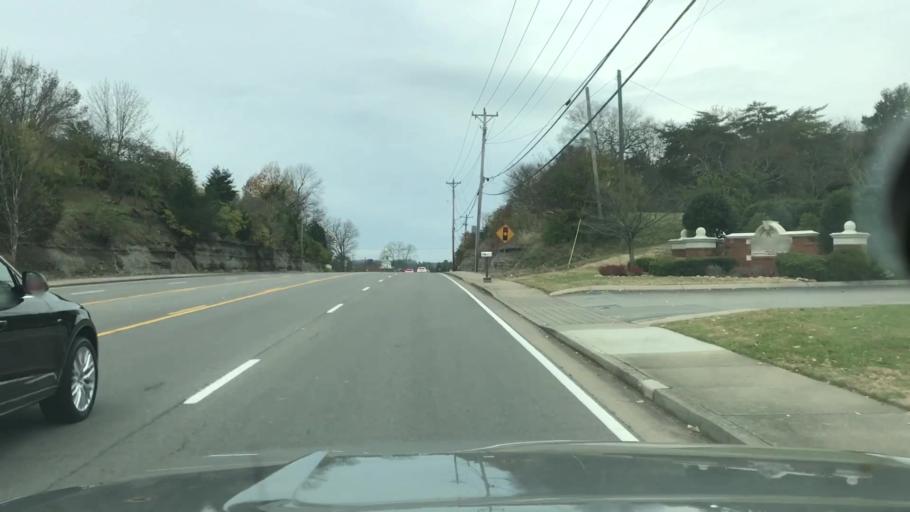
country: US
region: Tennessee
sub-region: Davidson County
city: Belle Meade
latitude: 36.0739
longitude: -86.9309
